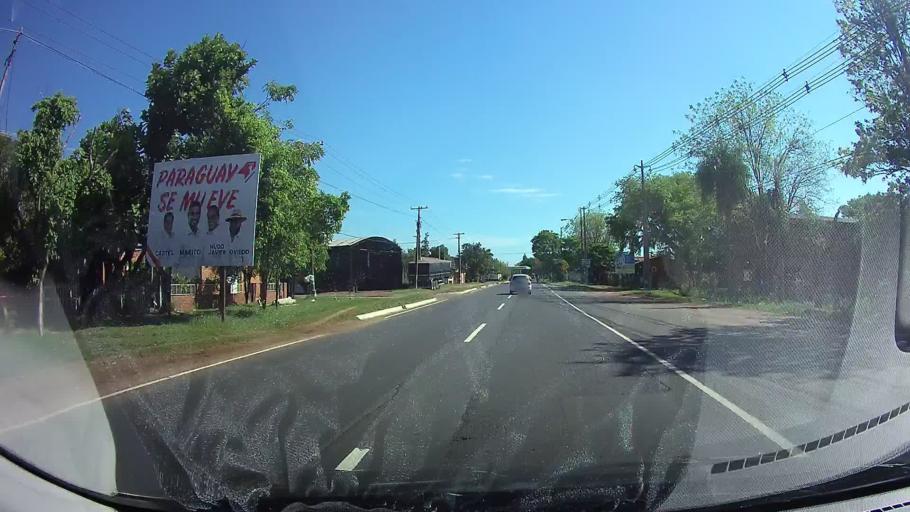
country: PY
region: Central
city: Ypacarai
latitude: -25.3965
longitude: -57.2813
